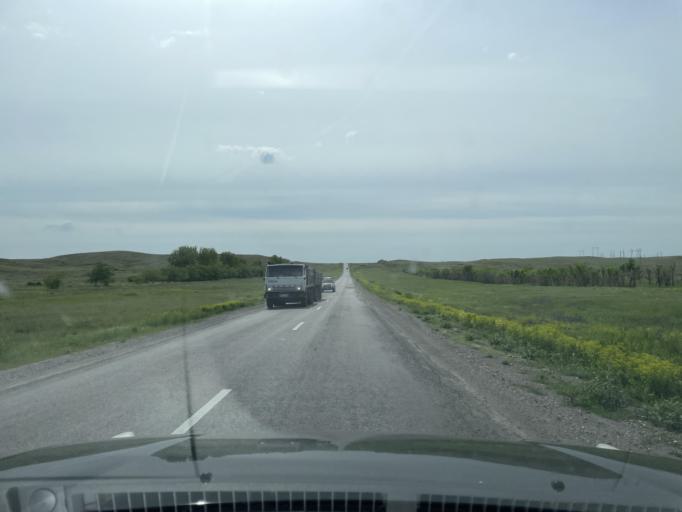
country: KZ
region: Qaraghandy
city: Abay
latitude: 49.4914
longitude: 72.9082
